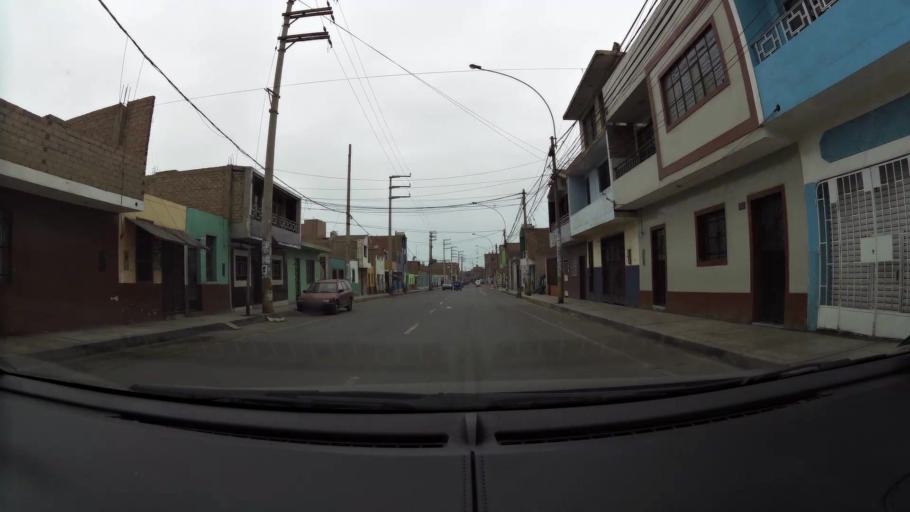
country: PE
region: Lima
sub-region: Barranca
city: Barranca
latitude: -10.7453
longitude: -77.7562
